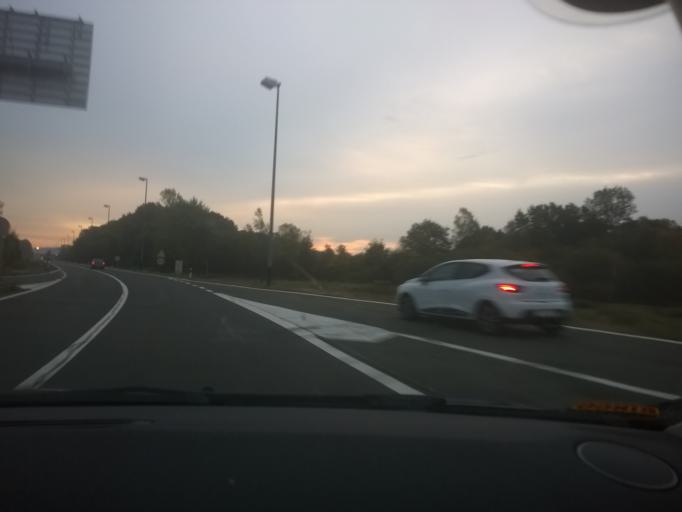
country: HR
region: Krapinsko-Zagorska
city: Oroslavje
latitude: 45.9990
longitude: 15.8683
